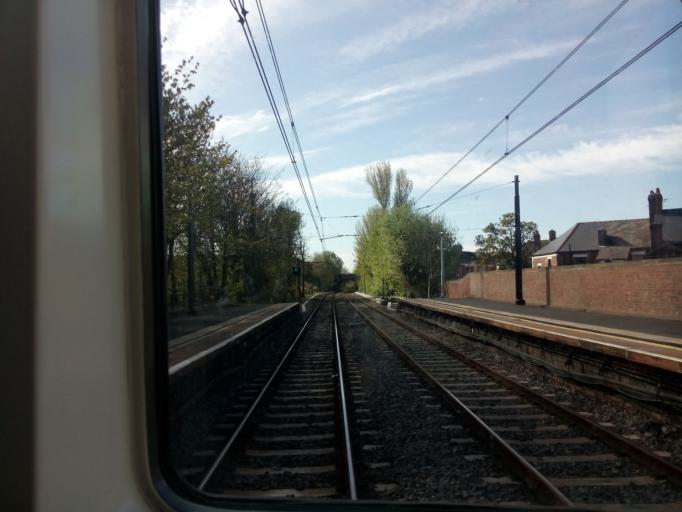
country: GB
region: England
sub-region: Newcastle upon Tyne
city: Gosforth
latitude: 54.9933
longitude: -1.6097
